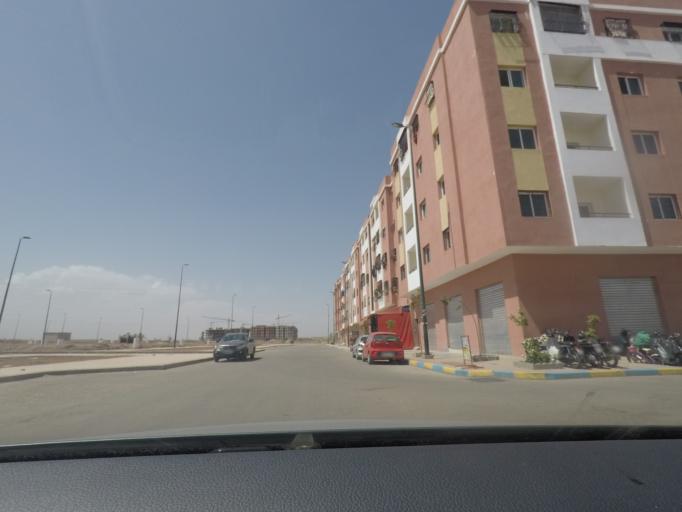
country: MA
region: Marrakech-Tensift-Al Haouz
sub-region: Marrakech
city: Marrakesh
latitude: 31.5833
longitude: -8.0380
